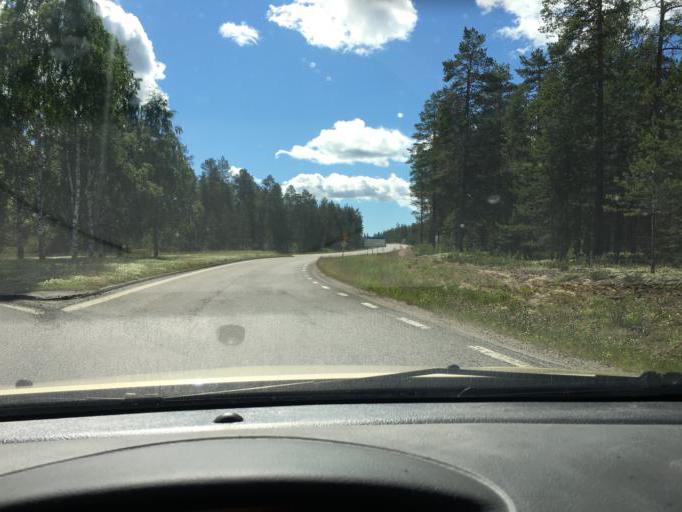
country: SE
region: Norrbotten
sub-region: Lulea Kommun
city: Bergnaset
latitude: 65.5801
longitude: 22.0734
